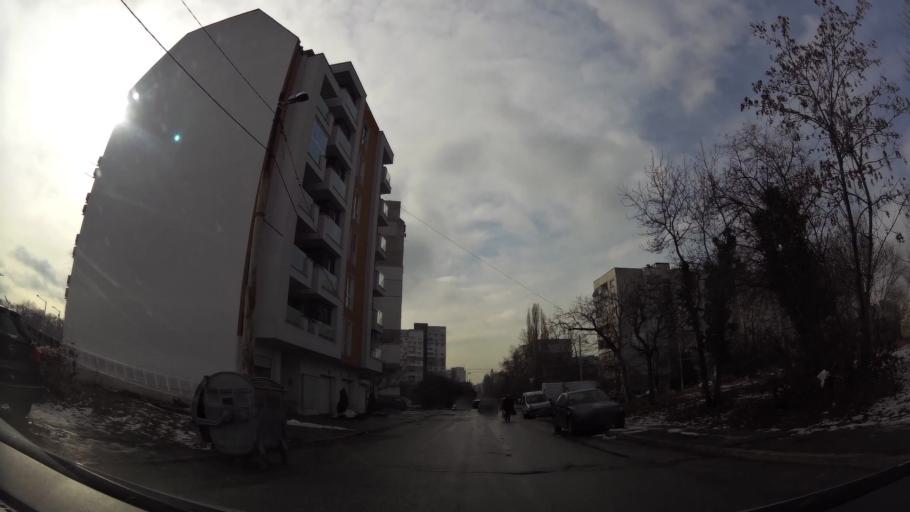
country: BG
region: Sofia-Capital
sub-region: Stolichna Obshtina
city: Sofia
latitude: 42.7166
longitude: 23.2767
